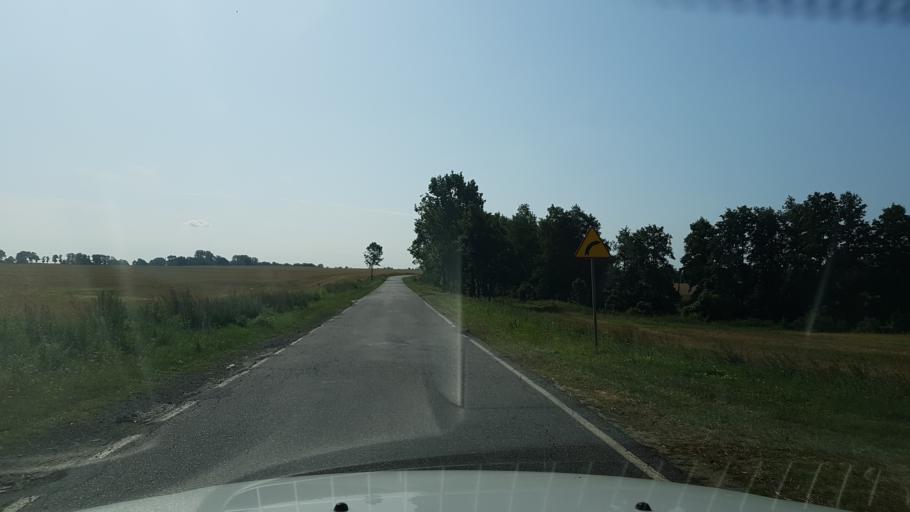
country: PL
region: West Pomeranian Voivodeship
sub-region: Powiat stargardzki
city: Dolice
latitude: 53.1325
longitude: 15.2519
